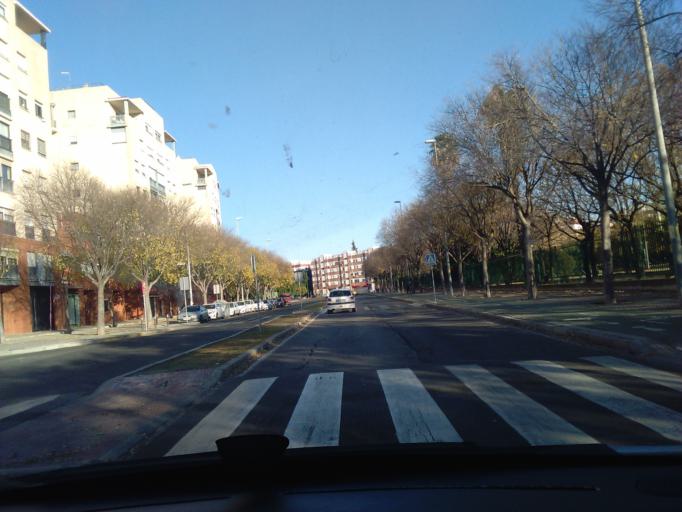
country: ES
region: Andalusia
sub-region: Provincia de Sevilla
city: Sevilla
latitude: 37.3664
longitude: -5.9736
